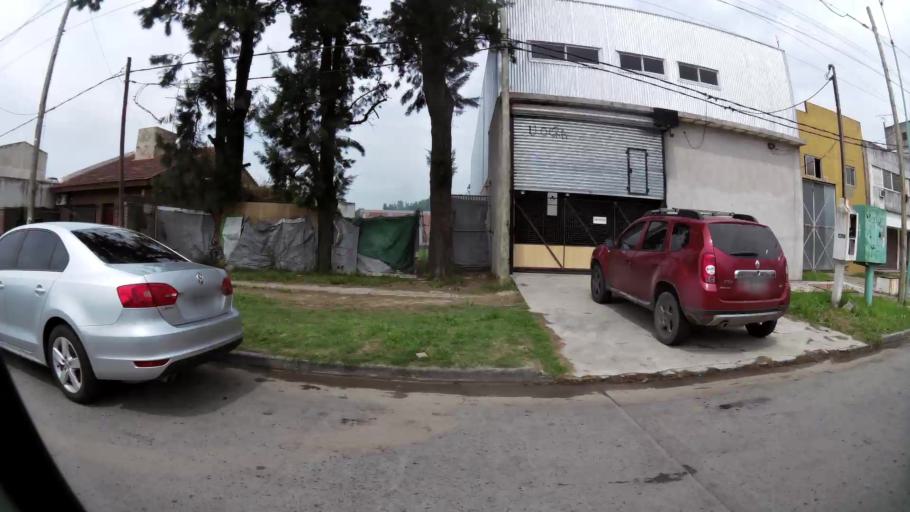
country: AR
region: Buenos Aires
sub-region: Partido de La Plata
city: La Plata
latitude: -34.9250
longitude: -58.0195
